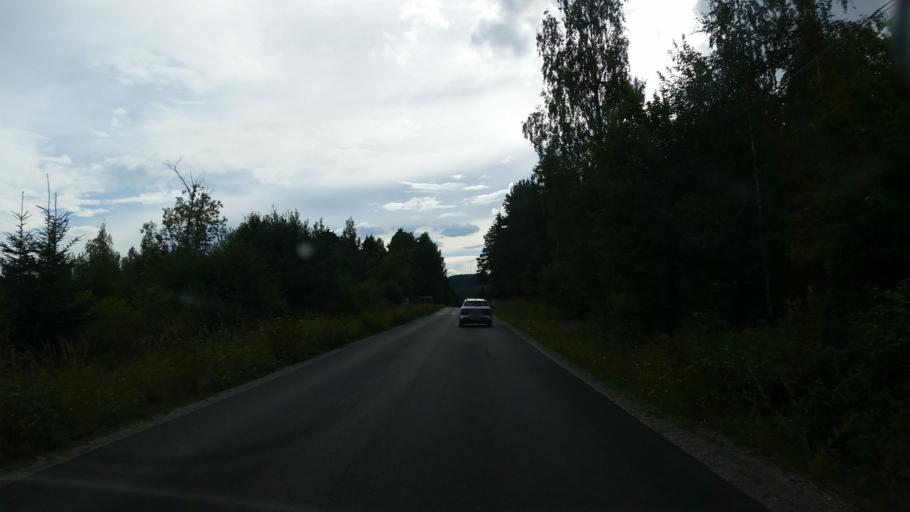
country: SE
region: Gaevleborg
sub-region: Hudiksvalls Kommun
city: Delsbo
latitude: 61.9077
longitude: 16.5673
